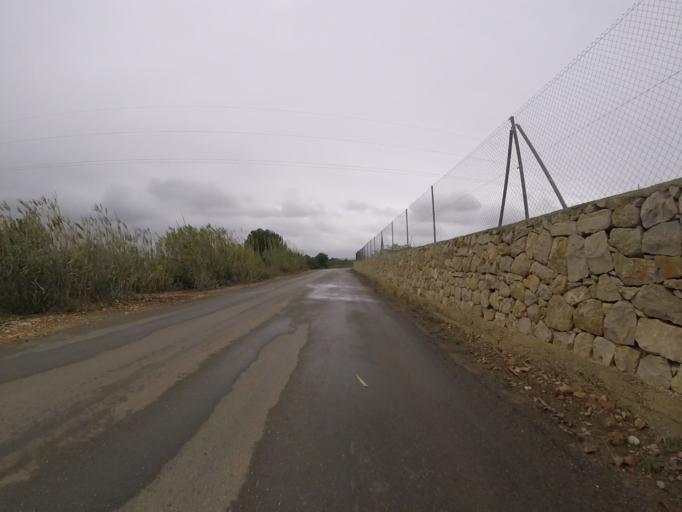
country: ES
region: Valencia
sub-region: Provincia de Castello
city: Alcoceber
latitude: 40.2398
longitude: 0.2495
